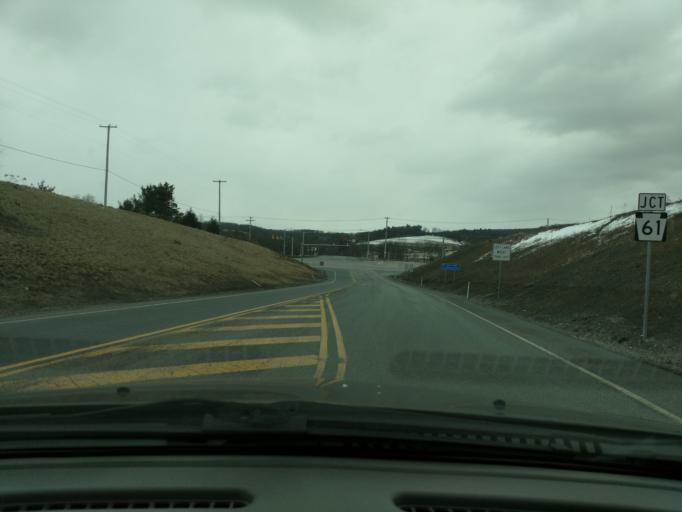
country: US
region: Pennsylvania
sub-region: Schuylkill County
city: Orwigsburg
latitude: 40.6299
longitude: -76.0651
